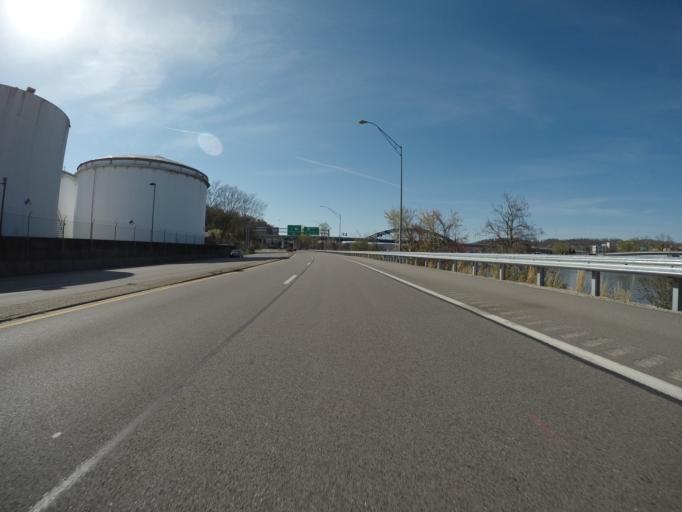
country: US
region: West Virginia
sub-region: Kanawha County
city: Charleston
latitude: 38.3521
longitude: -81.6454
